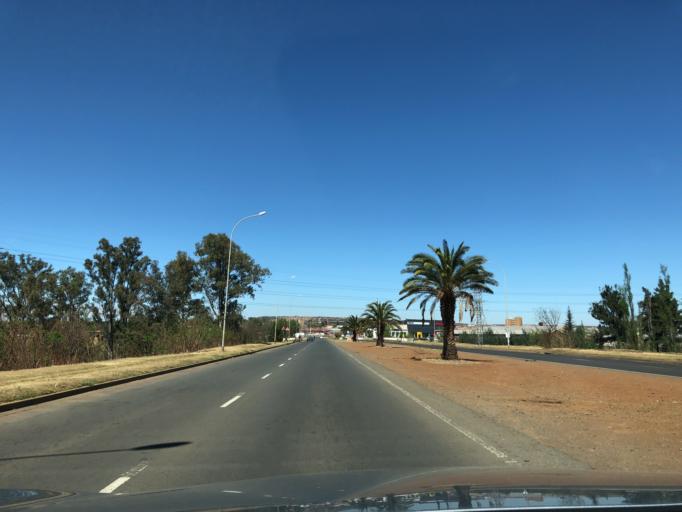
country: ZA
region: KwaZulu-Natal
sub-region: Amajuba District Municipality
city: Newcastle
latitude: -27.7459
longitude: 29.9375
